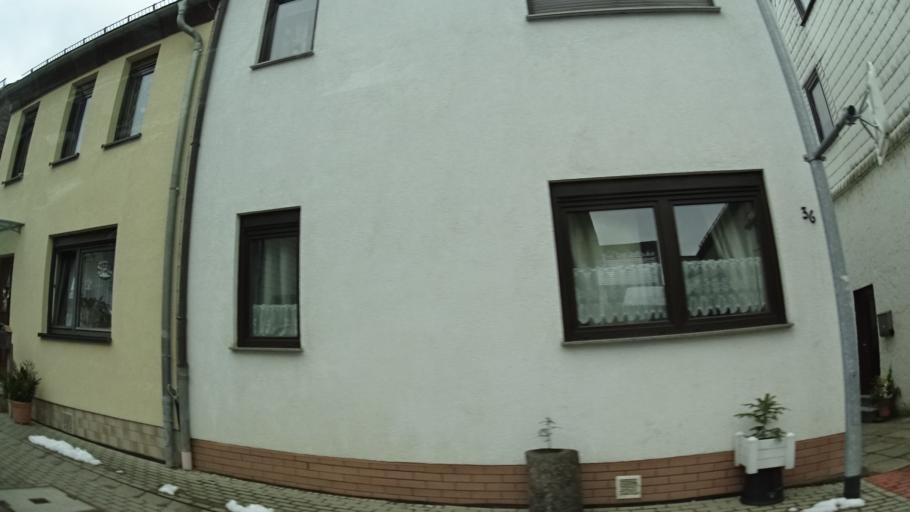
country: DE
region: Thuringia
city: Langewiesen
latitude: 50.6927
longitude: 10.9843
